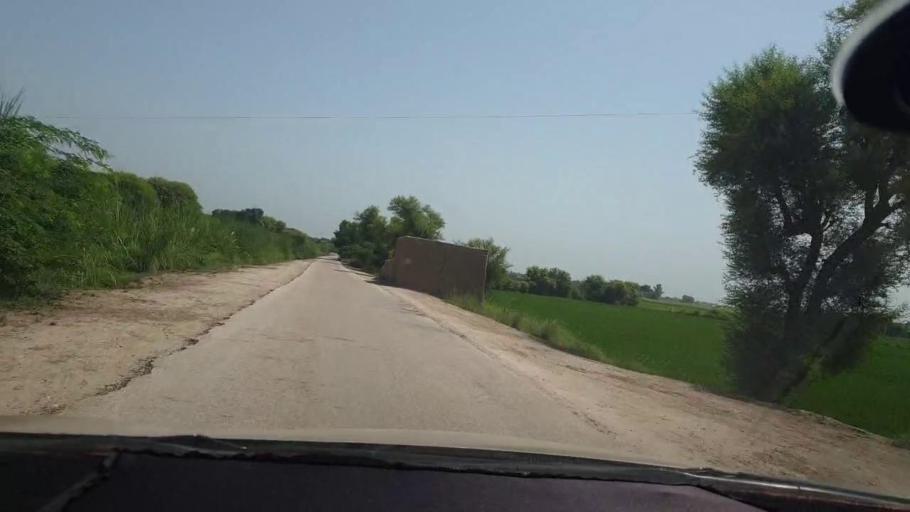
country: PK
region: Sindh
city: Kambar
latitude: 27.5212
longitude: 68.0083
